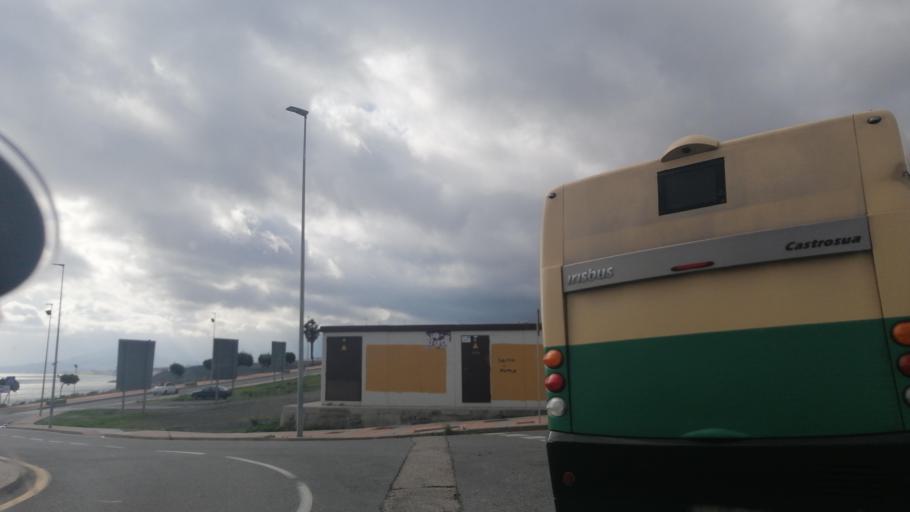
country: ES
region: Ceuta
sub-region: Ceuta
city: Ceuta
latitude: 35.8809
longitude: -5.3398
